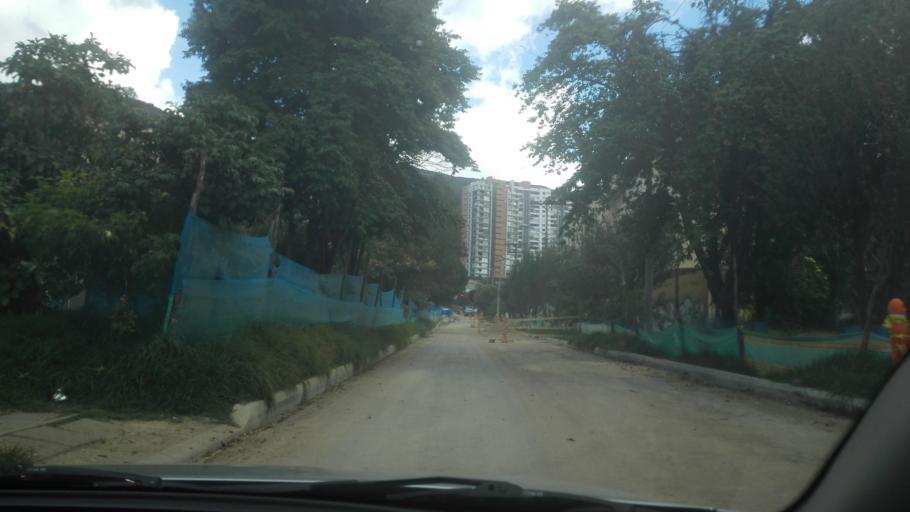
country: CO
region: Cundinamarca
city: La Calera
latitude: 4.7284
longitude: -74.0268
